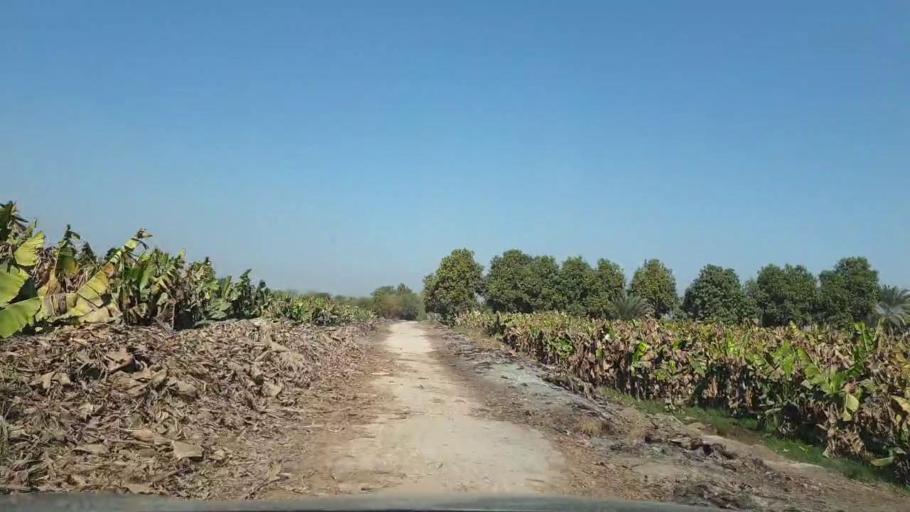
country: PK
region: Sindh
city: Tando Adam
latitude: 25.6348
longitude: 68.6752
